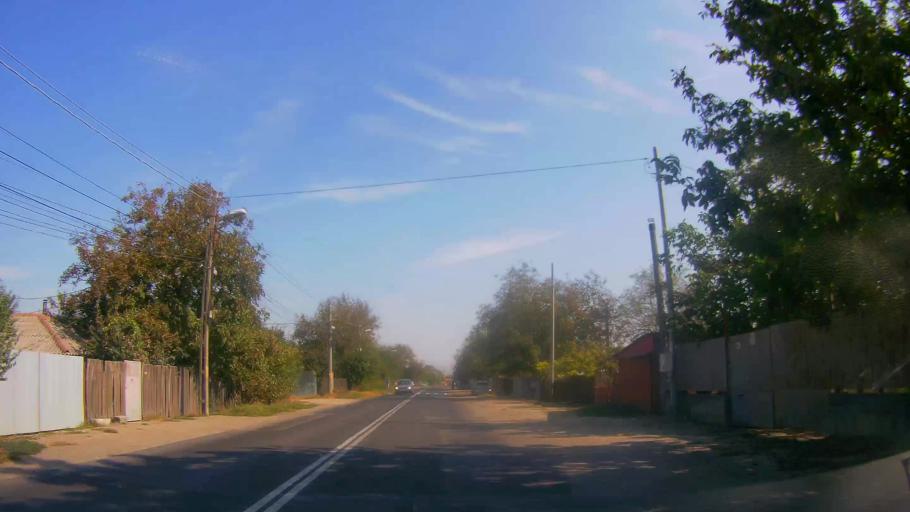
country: RO
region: Giurgiu
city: Giurgiu
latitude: 43.9104
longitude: 25.9830
